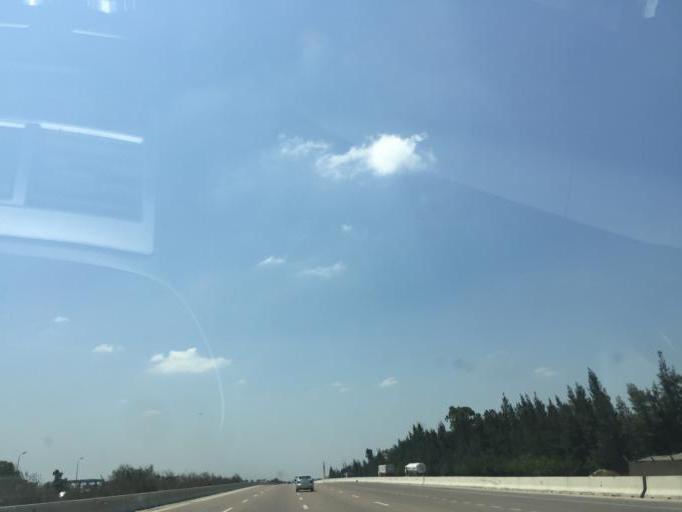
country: EG
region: Al Buhayrah
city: Abu al Matamir
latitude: 30.6772
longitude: 30.0738
